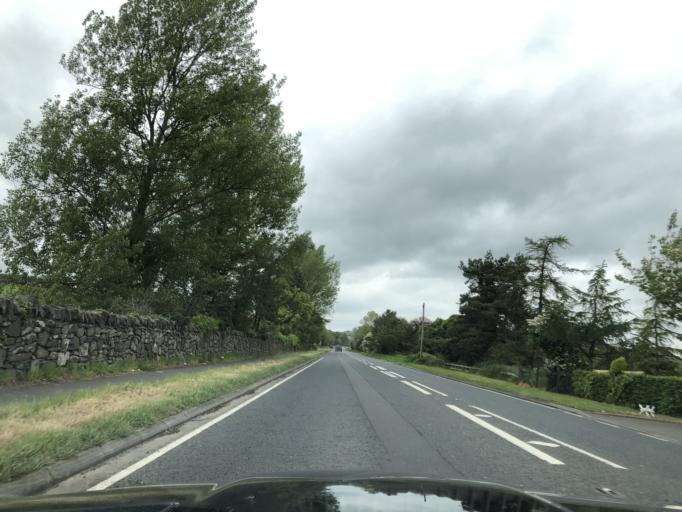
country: GB
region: Northern Ireland
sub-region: Down District
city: Downpatrick
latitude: 54.3492
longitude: -5.7359
